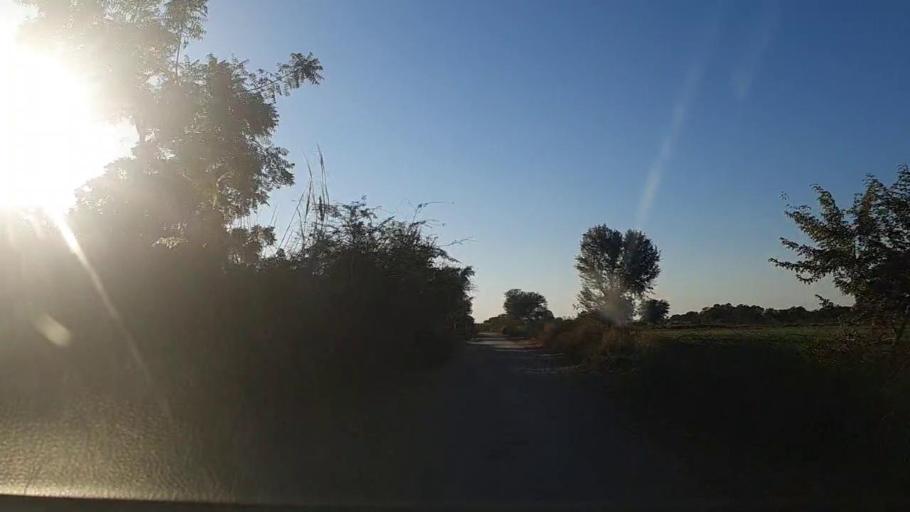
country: PK
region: Sindh
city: Sanghar
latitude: 26.1392
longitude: 68.9378
